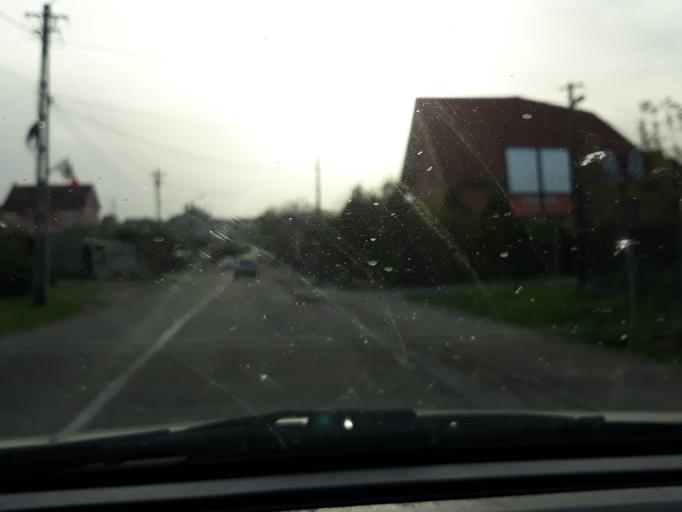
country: RO
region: Bihor
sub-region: Comuna Sanmartin
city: Sanmartin
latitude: 47.0012
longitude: 21.9880
